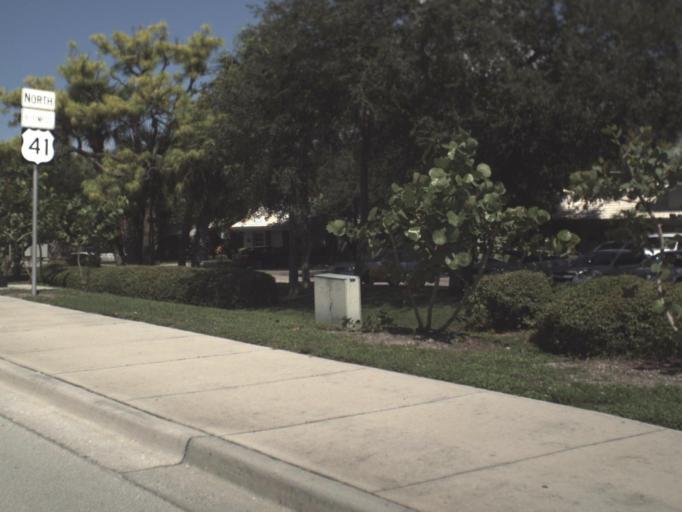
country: US
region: Florida
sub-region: Sarasota County
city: Venice Gardens
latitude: 27.0776
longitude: -82.4282
